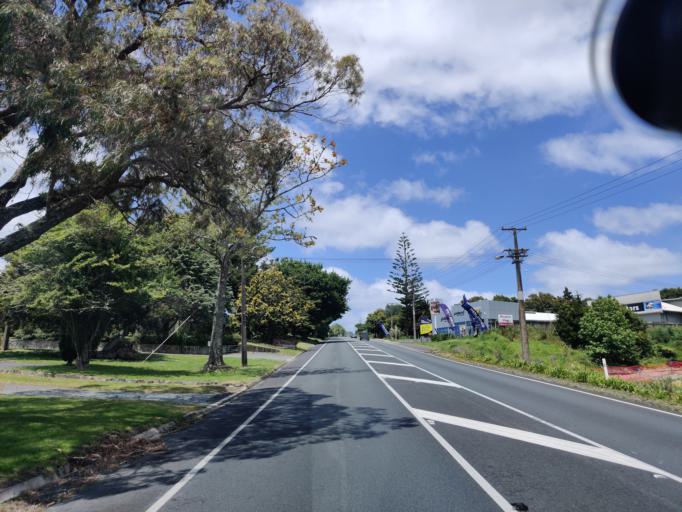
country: NZ
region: Auckland
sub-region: Auckland
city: Wellsford
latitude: -36.2825
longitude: 174.5194
